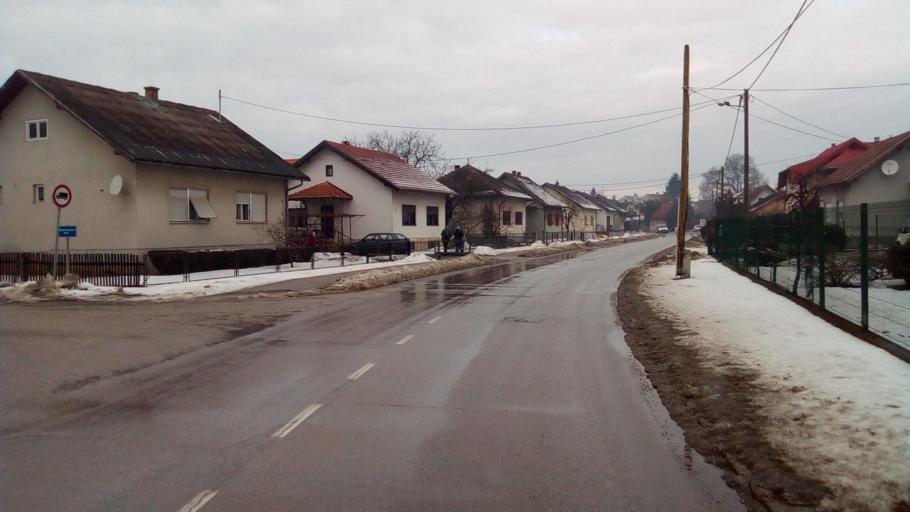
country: HR
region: Zagrebacka
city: Lupoglav
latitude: 45.7007
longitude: 16.3957
